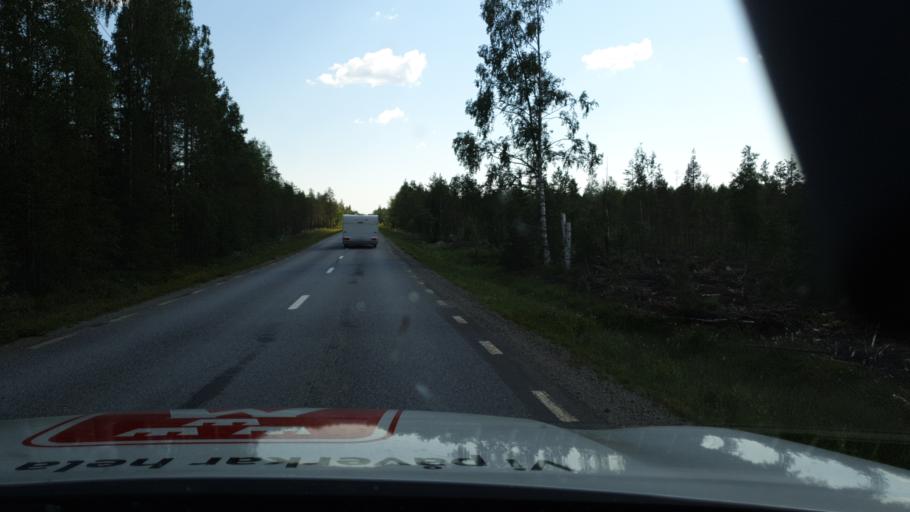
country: SE
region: Vaesterbotten
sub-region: Skelleftea Kommun
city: Burtraesk
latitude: 64.3711
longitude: 20.2491
